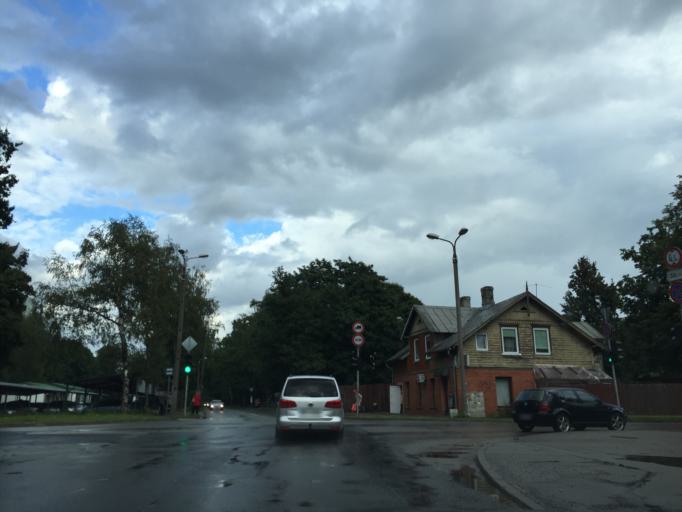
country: LV
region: Marupe
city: Marupe
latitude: 56.9532
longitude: 23.9973
